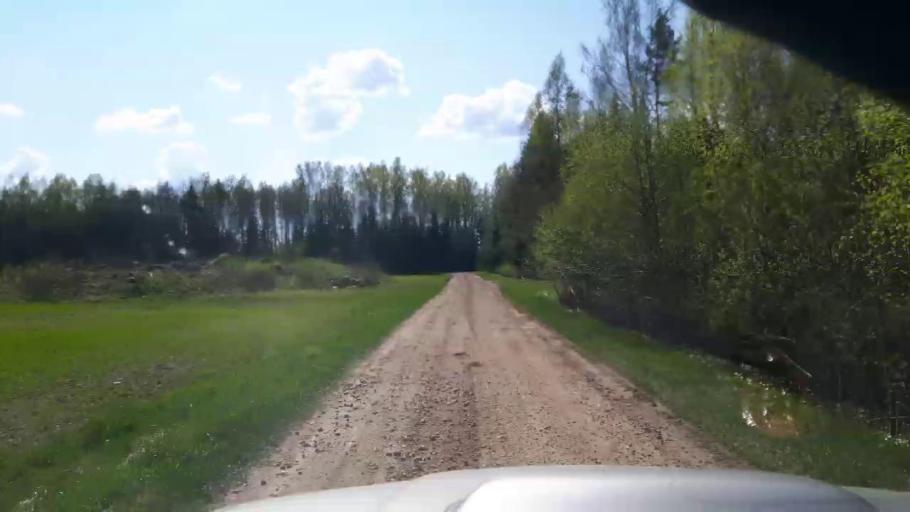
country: EE
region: Paernumaa
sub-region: Tootsi vald
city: Tootsi
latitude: 58.4969
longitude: 24.9424
